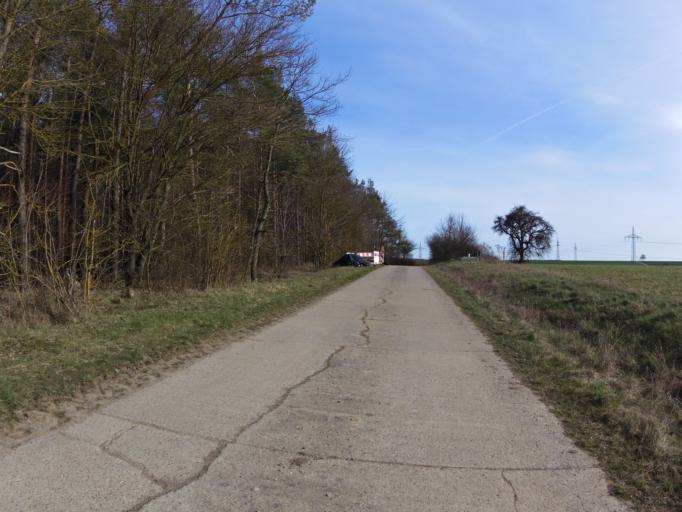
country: DE
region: Bavaria
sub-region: Regierungsbezirk Unterfranken
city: Hettstadt
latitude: 49.8191
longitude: 9.8286
